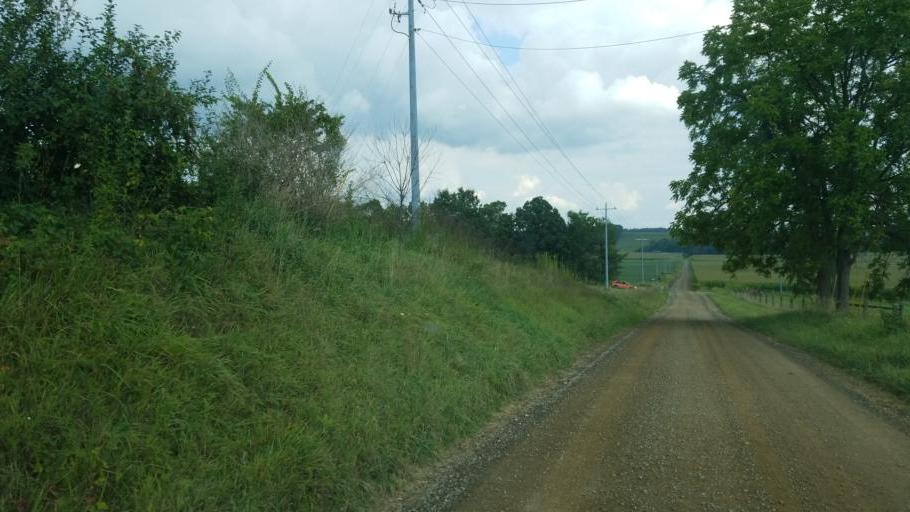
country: US
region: Ohio
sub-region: Knox County
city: Oak Hill
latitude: 40.4219
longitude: -82.2561
